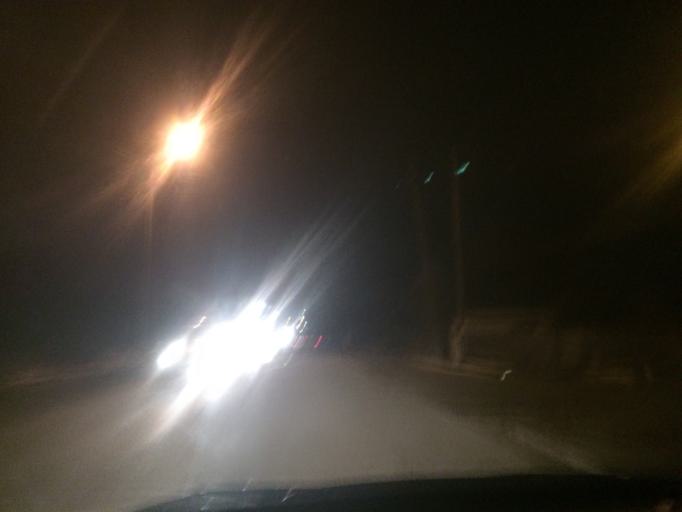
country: KZ
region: Astana Qalasy
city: Astana
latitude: 51.2089
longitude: 71.3812
